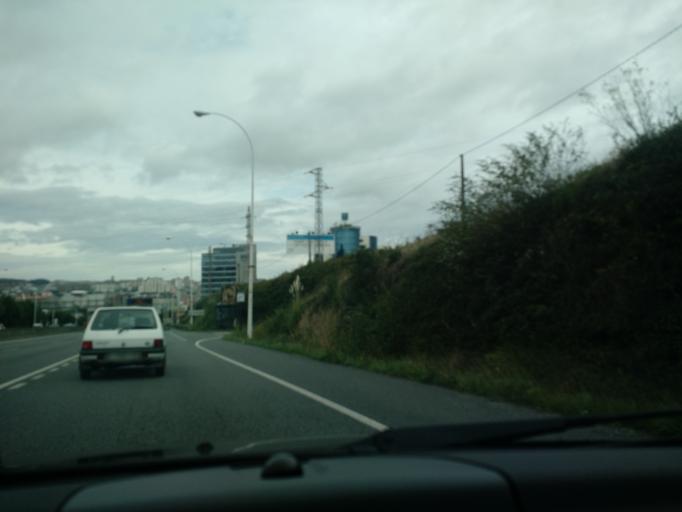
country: ES
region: Galicia
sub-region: Provincia da Coruna
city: A Coruna
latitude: 43.3354
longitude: -8.4031
